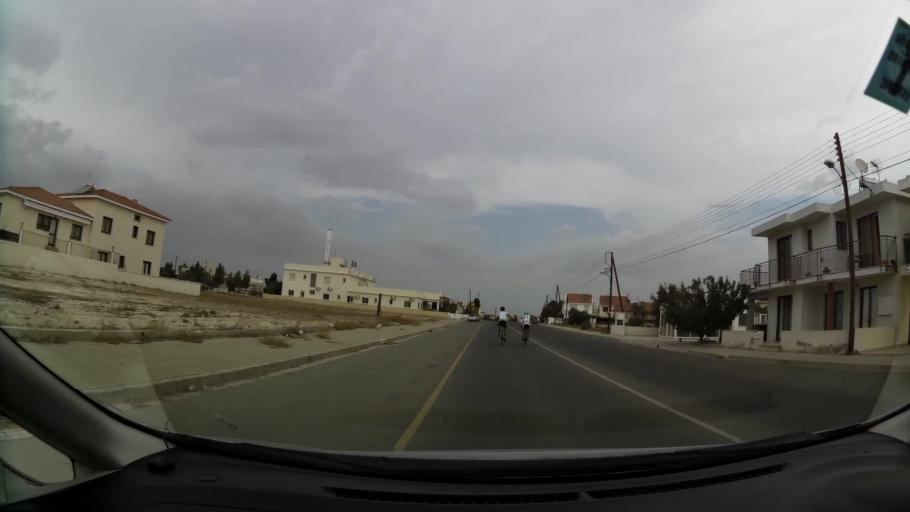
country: CY
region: Lefkosia
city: Geri
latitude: 35.0973
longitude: 33.3887
